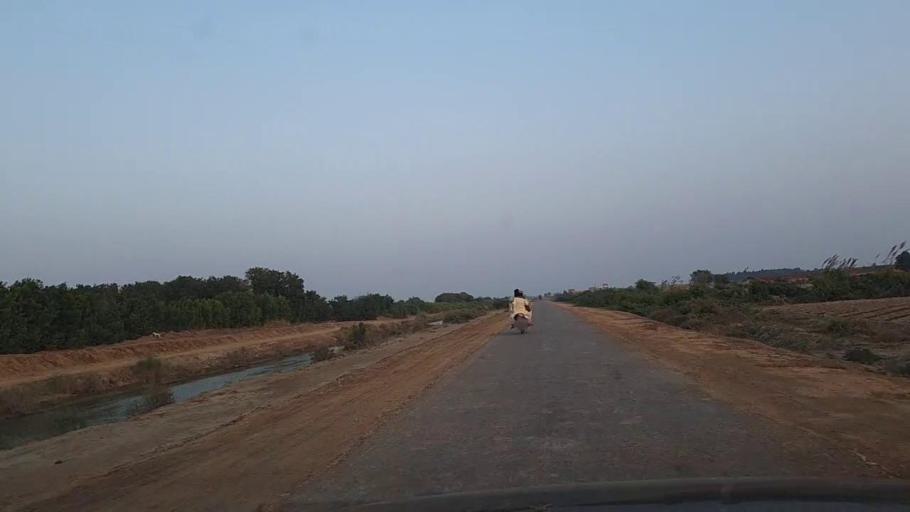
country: PK
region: Sindh
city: Mirpur Sakro
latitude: 24.6361
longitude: 67.6030
